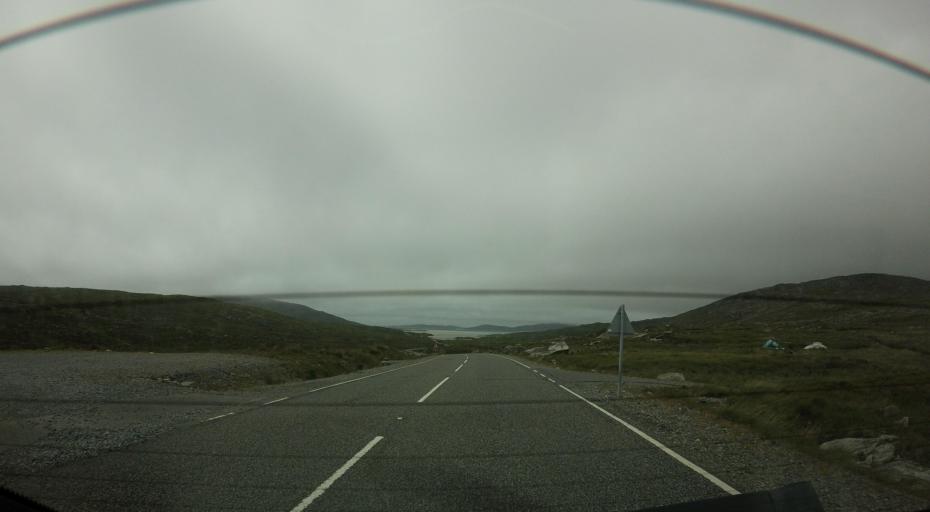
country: GB
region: Scotland
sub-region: Eilean Siar
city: Harris
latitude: 57.8662
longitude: -6.8819
